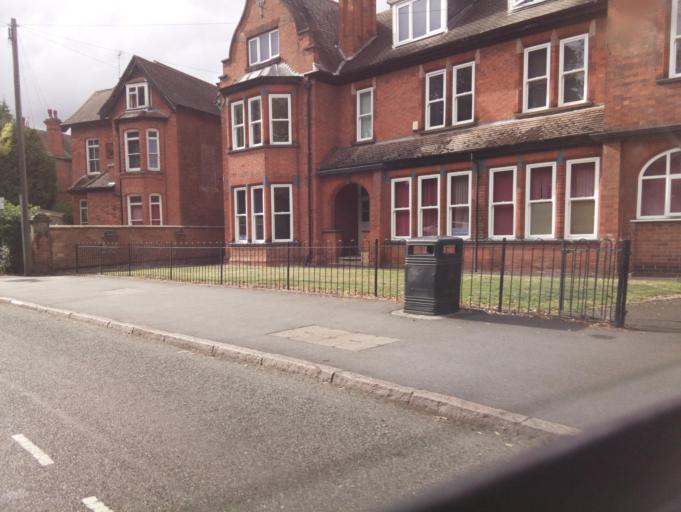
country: GB
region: England
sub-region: Leicestershire
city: Loughborough
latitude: 52.7723
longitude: -1.2201
